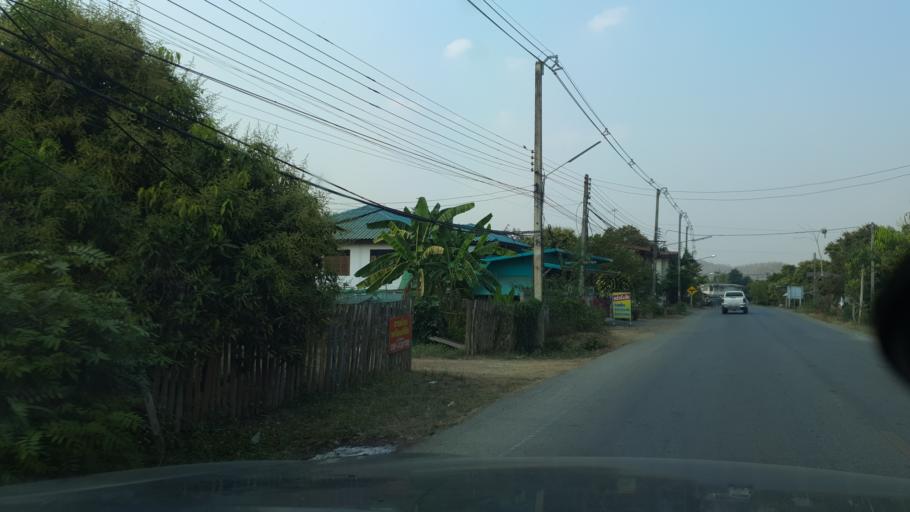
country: TH
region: Sukhothai
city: Thung Saliam
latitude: 17.3202
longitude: 99.5369
